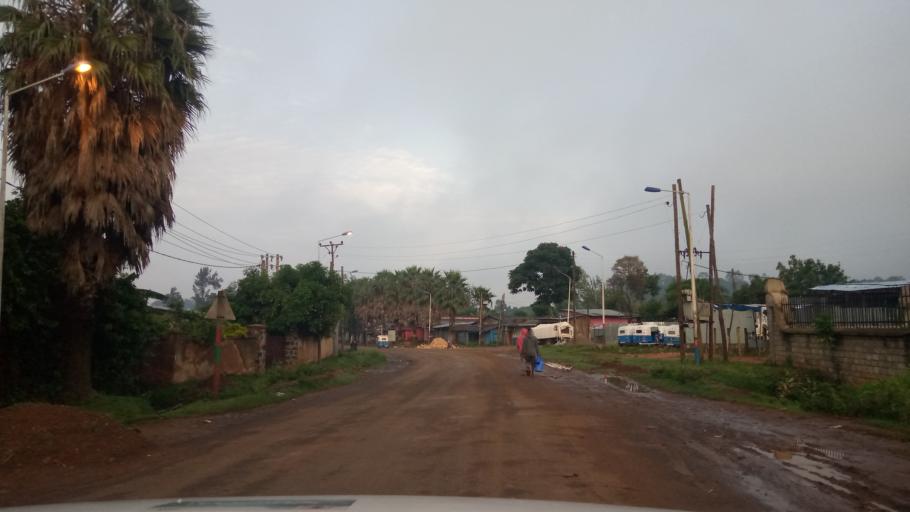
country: ET
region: Oromiya
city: Jima
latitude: 7.6827
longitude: 36.8429
